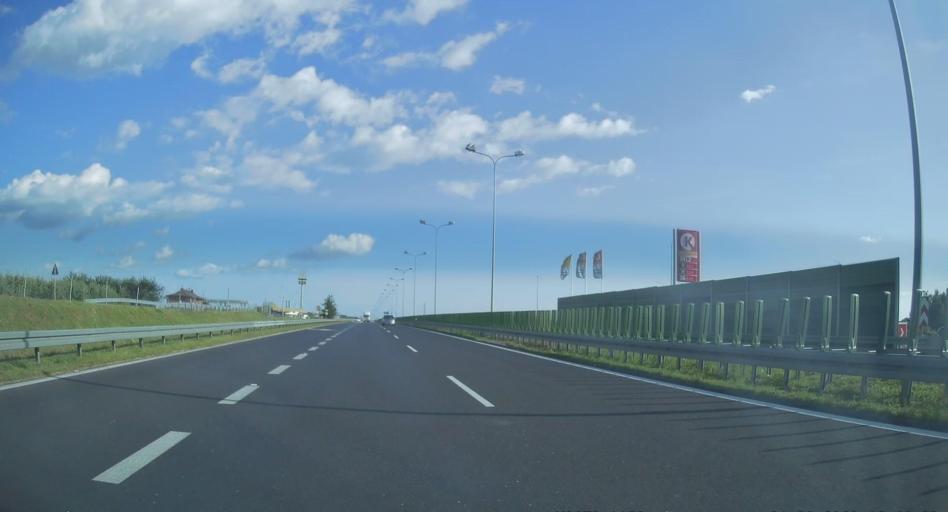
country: PL
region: Masovian Voivodeship
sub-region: Powiat grojecki
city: Goszczyn
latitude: 51.7476
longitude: 20.9097
